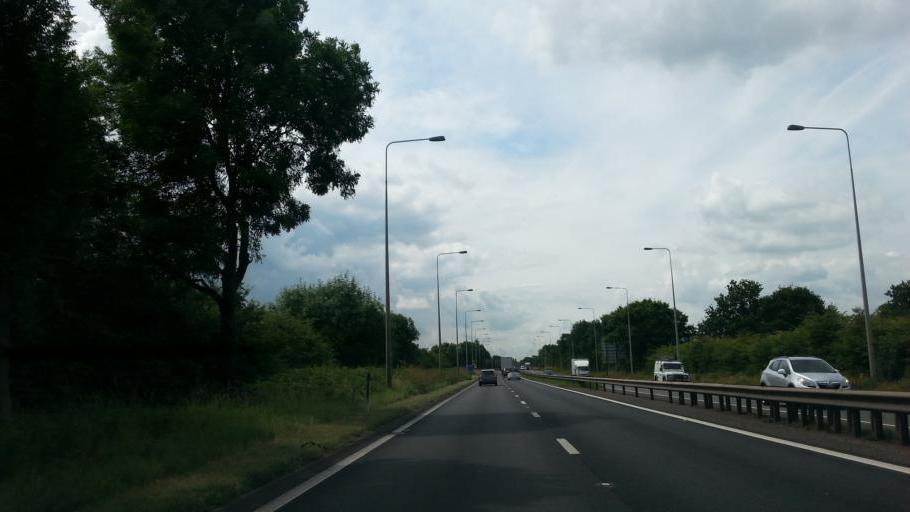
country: GB
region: England
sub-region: Staffordshire
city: Alrewas
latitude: 52.7233
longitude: -1.7505
